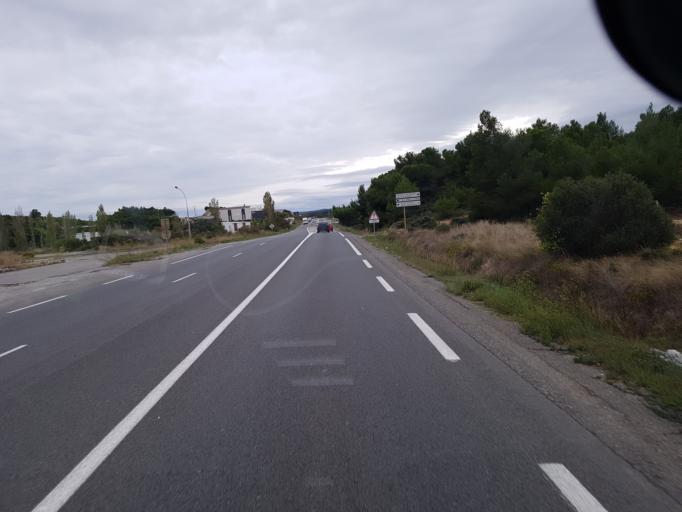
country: FR
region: Languedoc-Roussillon
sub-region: Departement de l'Aude
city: Peyriac-de-Mer
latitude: 43.1308
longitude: 2.9629
